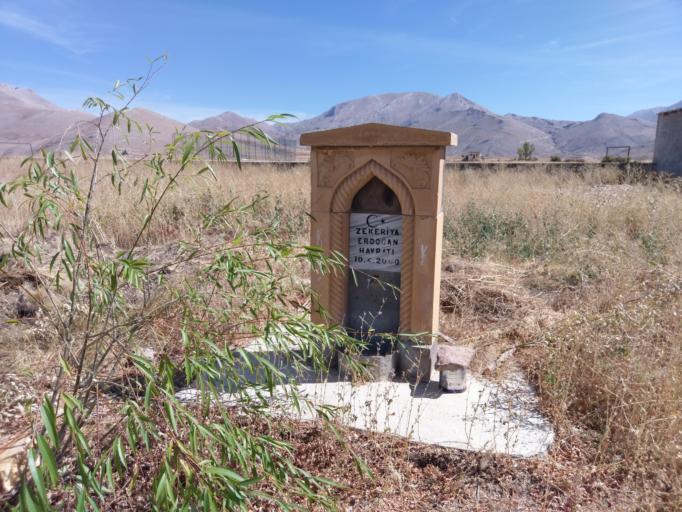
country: TR
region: Kayseri
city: Toklar
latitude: 38.4076
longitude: 36.0846
